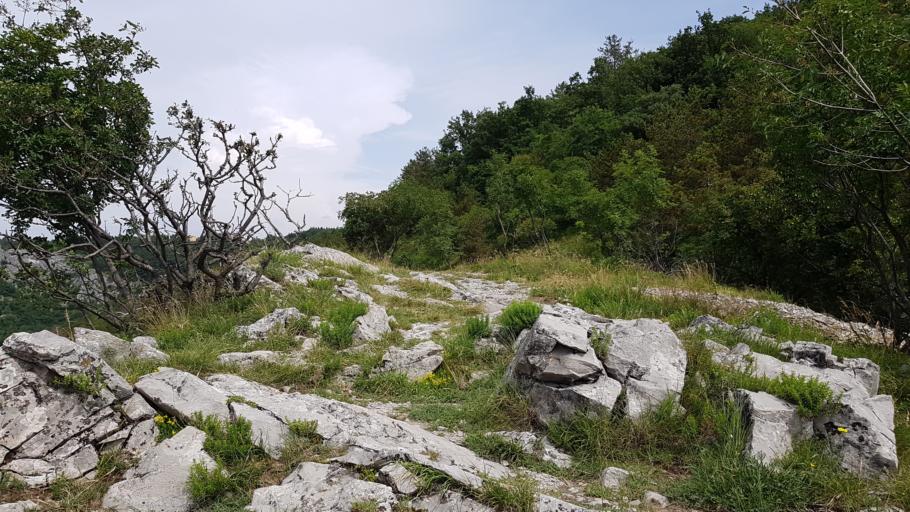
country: IT
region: Friuli Venezia Giulia
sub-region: Provincia di Trieste
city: Dolina
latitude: 45.6213
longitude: 13.8759
